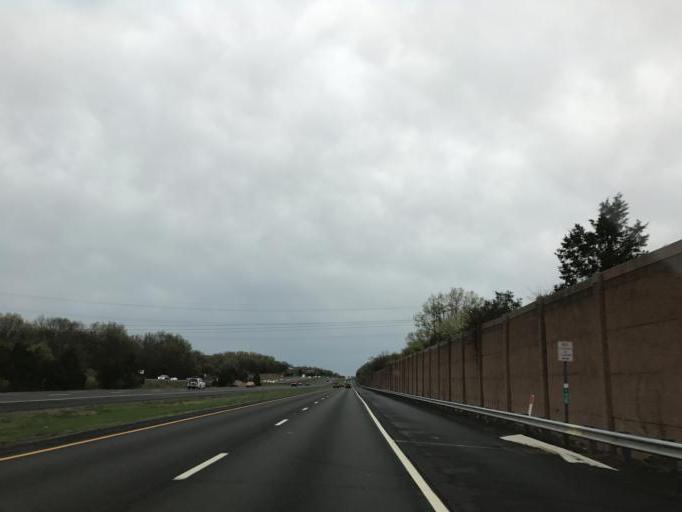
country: US
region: New Jersey
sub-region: Somerset County
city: Bridgewater
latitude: 40.6194
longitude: -74.6373
